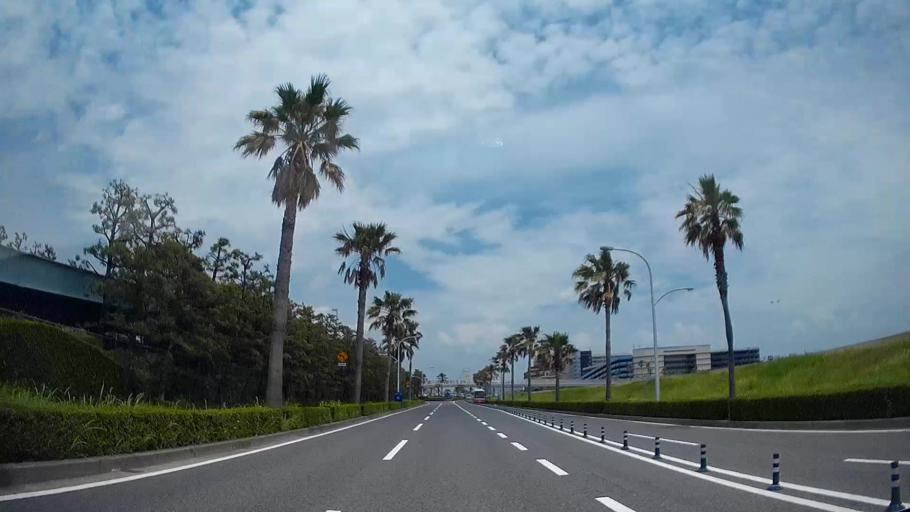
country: JP
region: Tokyo
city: Urayasu
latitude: 35.6247
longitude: 139.8908
